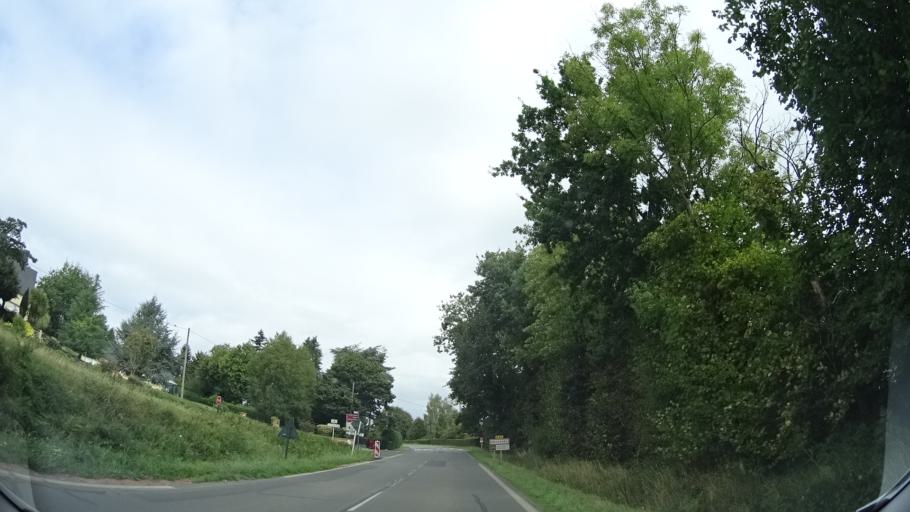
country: FR
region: Brittany
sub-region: Departement d'Ille-et-Vilaine
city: Irodouer
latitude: 48.2984
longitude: -1.9376
